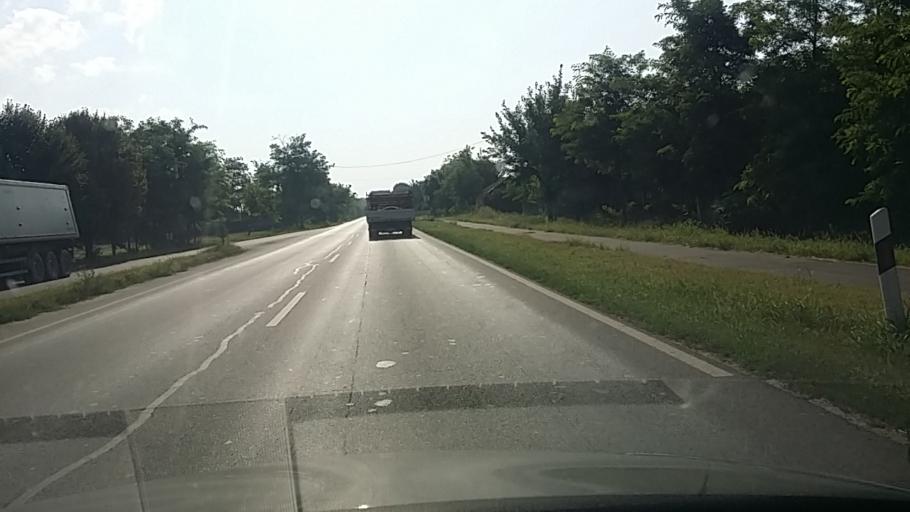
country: HU
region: Bekes
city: Kondoros
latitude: 46.7496
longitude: 20.8383
